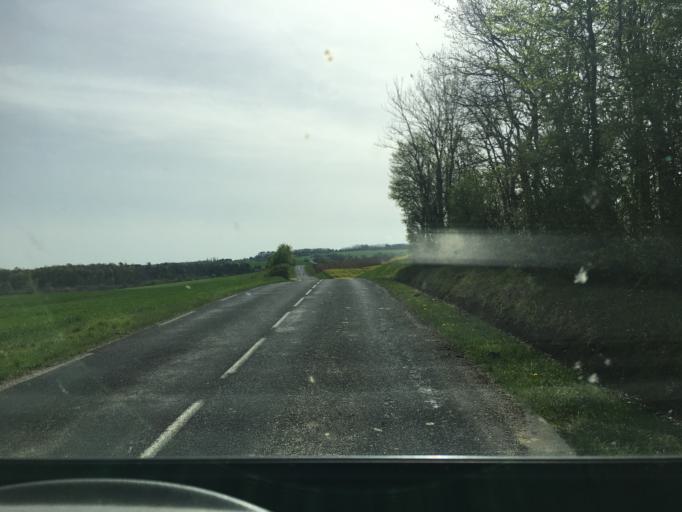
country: FR
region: Lorraine
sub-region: Departement de Meurthe-et-Moselle
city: Gondreville
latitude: 48.6665
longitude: 5.9491
